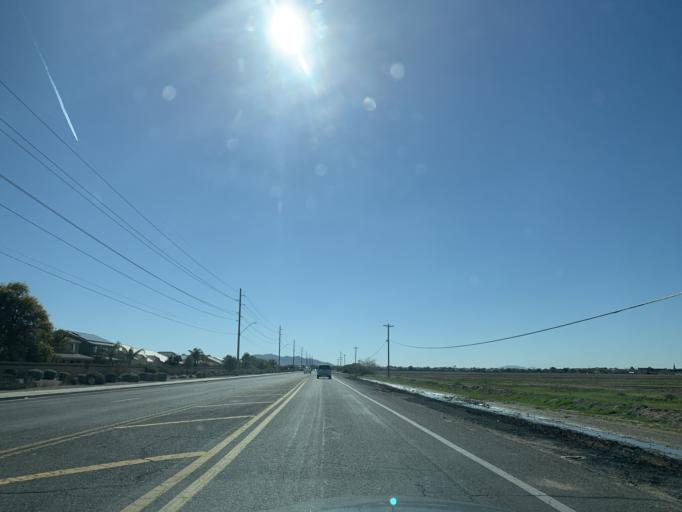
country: US
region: Arizona
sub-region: Pinal County
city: Casa Grande
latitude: 32.9013
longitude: -111.7226
